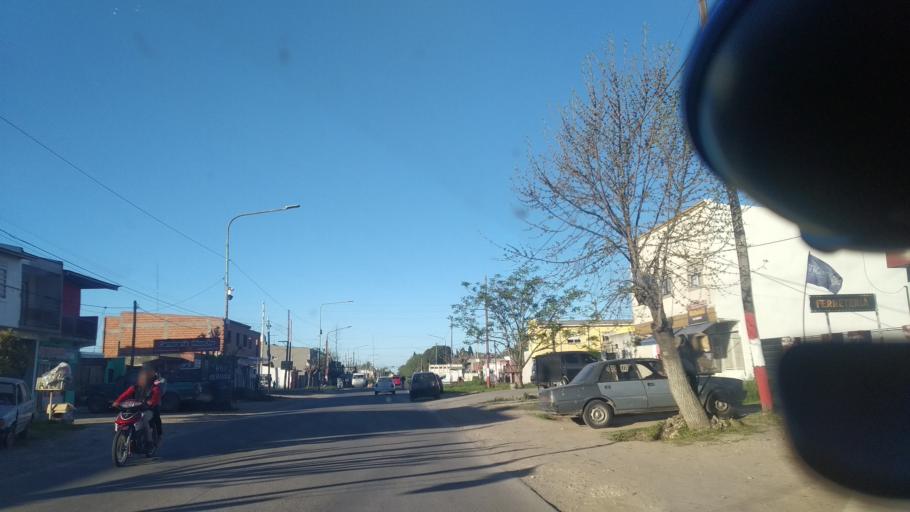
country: AR
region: Buenos Aires
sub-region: Partido de La Plata
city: La Plata
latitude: -34.9621
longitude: -57.9620
